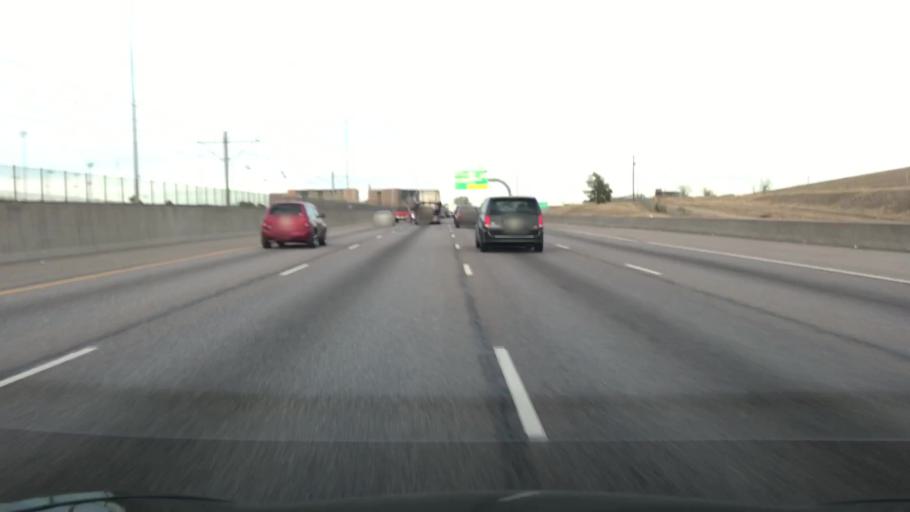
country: US
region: Colorado
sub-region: Arapahoe County
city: Centennial
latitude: 39.6527
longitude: -104.8568
